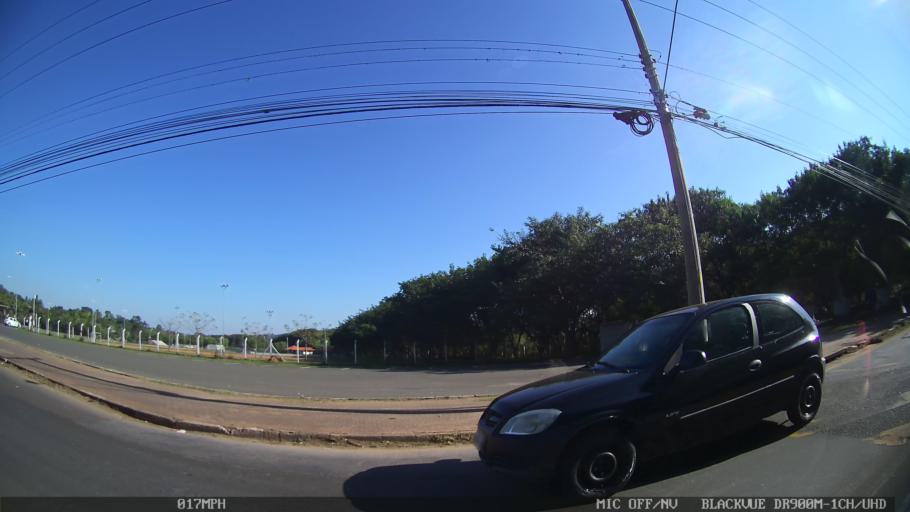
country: BR
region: Sao Paulo
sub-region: Campinas
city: Campinas
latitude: -22.9608
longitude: -47.1060
